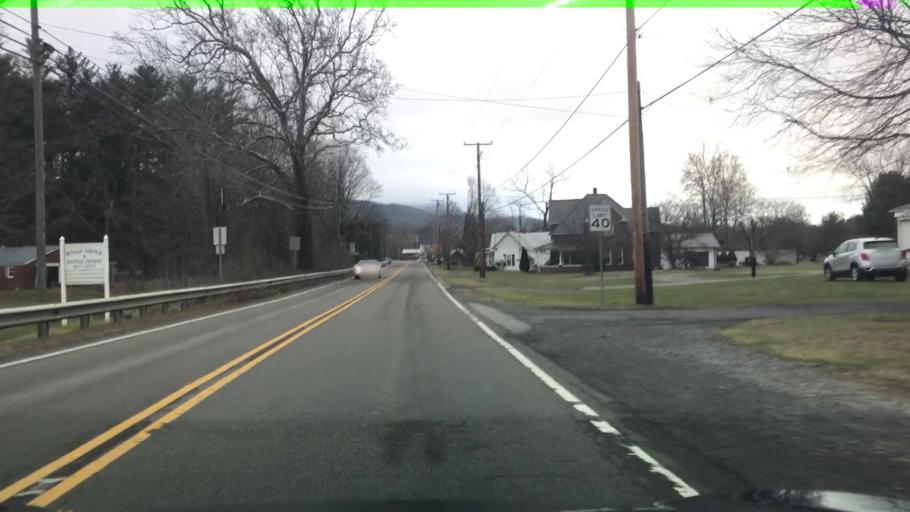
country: US
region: Virginia
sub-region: Smyth County
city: Atkins
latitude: 36.7776
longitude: -81.4096
